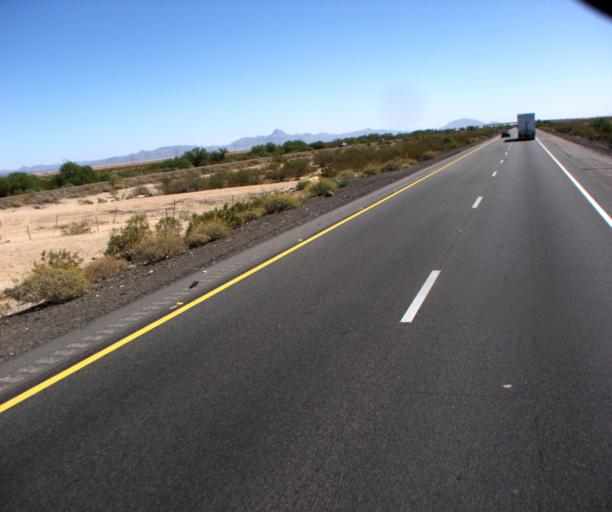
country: US
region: Arizona
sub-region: La Paz County
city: Salome
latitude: 33.5713
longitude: -113.3702
